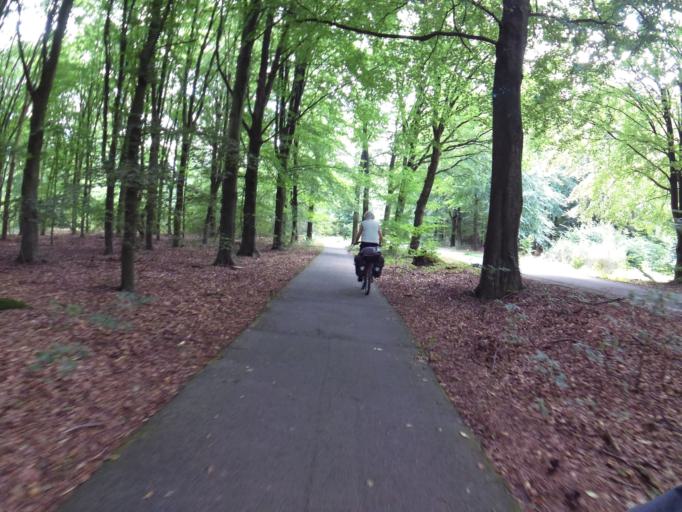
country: NL
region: Drenthe
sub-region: Gemeente Borger-Odoorn
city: Borger
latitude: 52.9593
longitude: 6.7585
